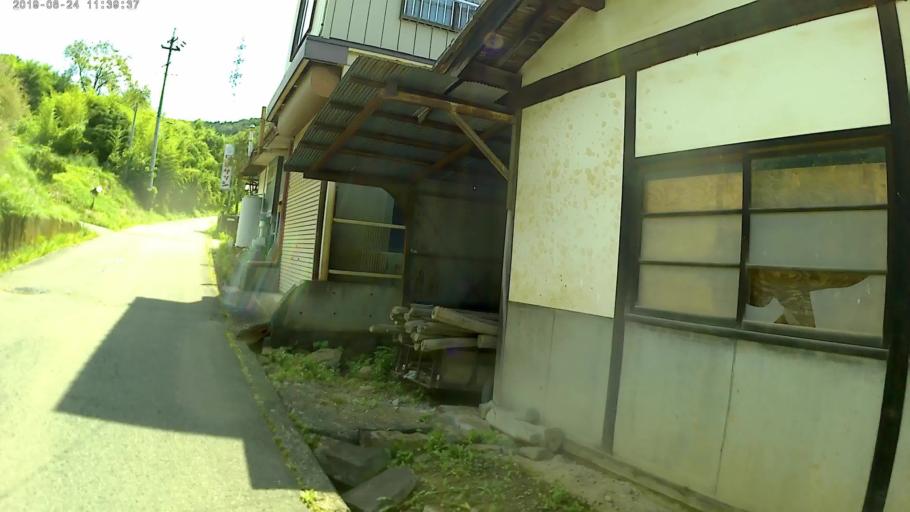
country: JP
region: Nagano
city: Kamimaruko
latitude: 36.2726
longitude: 138.3412
